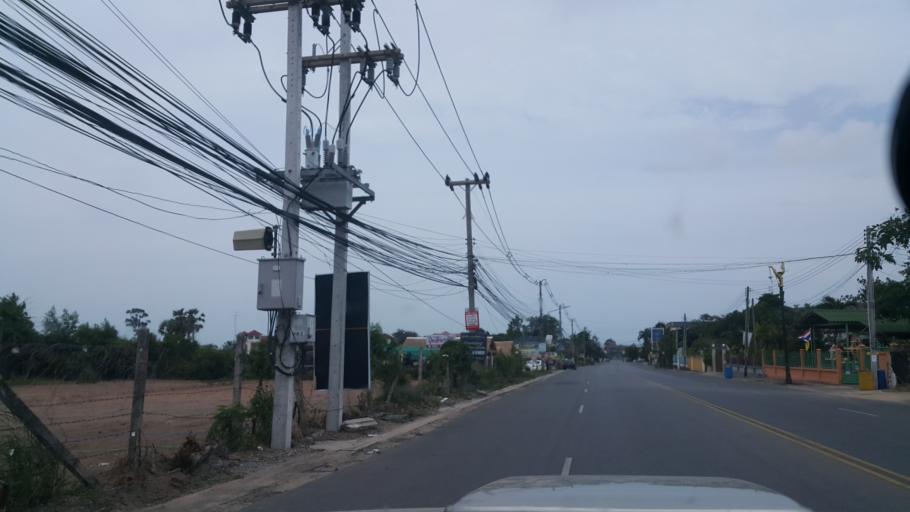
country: TH
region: Rayong
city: Ban Chang
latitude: 12.7163
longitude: 101.0493
